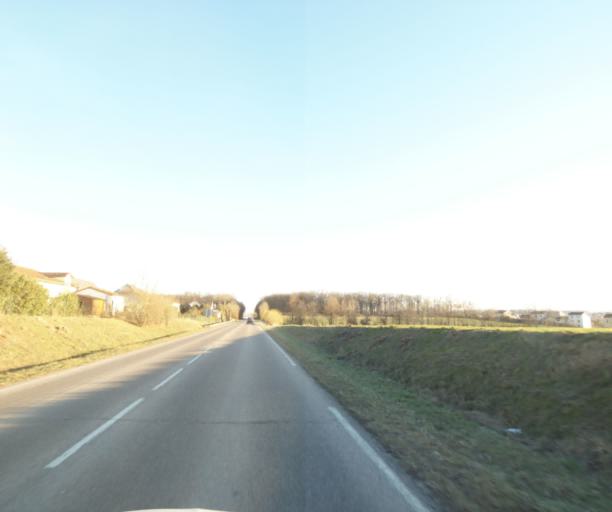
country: FR
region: Lorraine
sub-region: Departement de Meurthe-et-Moselle
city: Tomblaine
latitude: 48.6744
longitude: 6.2284
